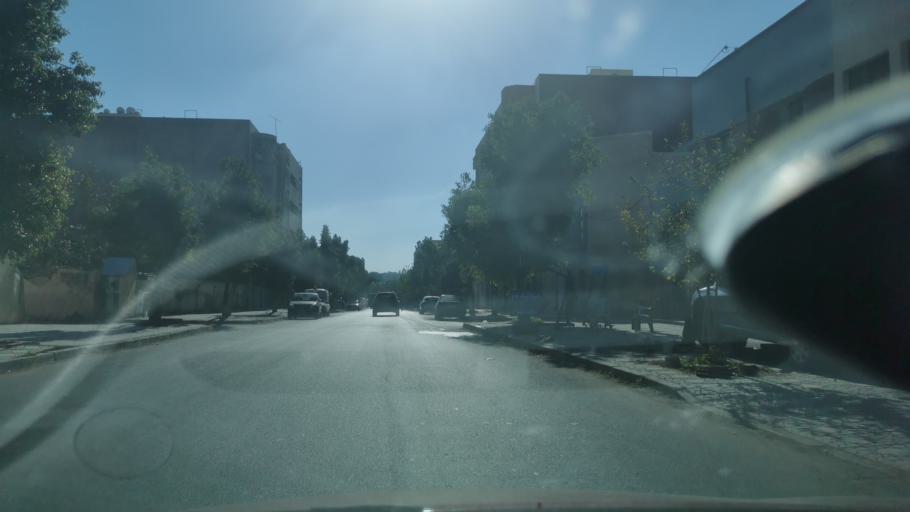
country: MA
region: Fes-Boulemane
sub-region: Fes
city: Fes
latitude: 34.0356
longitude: -4.9905
